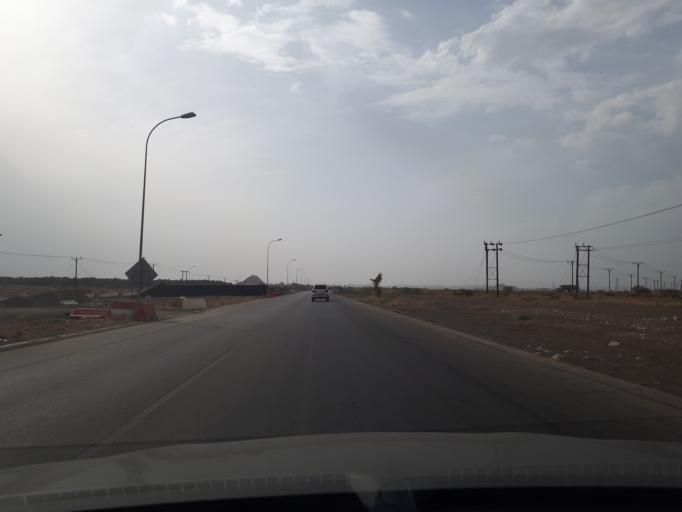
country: OM
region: Ash Sharqiyah
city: Al Qabil
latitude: 22.5640
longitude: 58.7064
